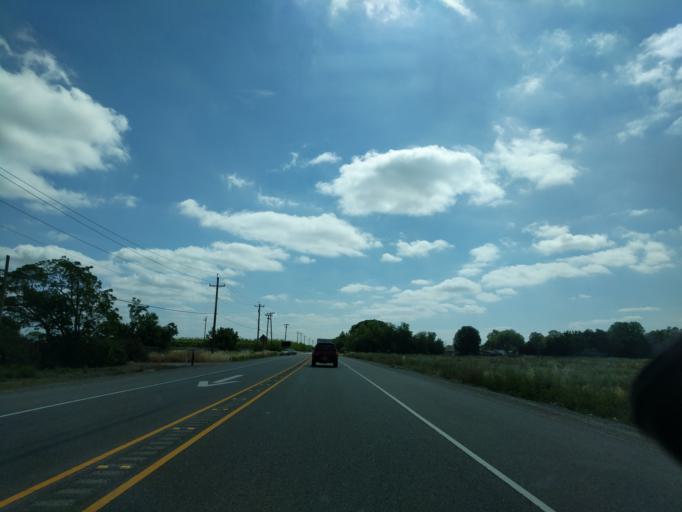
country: US
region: California
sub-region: Contra Costa County
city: Brentwood
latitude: 37.8963
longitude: -121.6928
